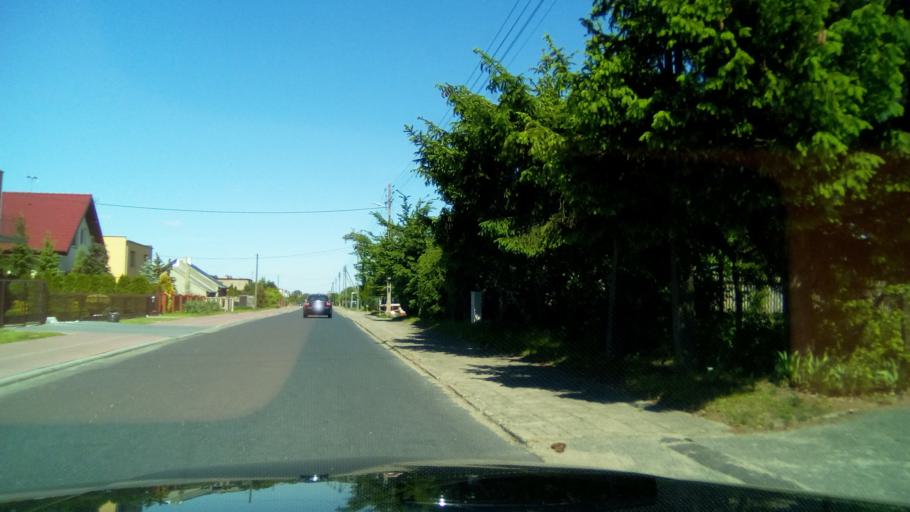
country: PL
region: Greater Poland Voivodeship
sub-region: Powiat gnieznienski
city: Niechanowo
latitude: 52.4627
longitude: 17.6713
